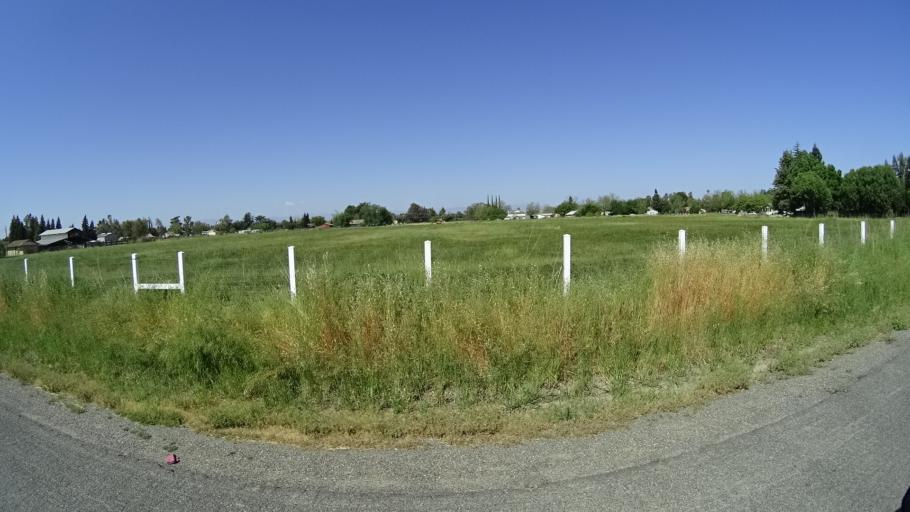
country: US
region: California
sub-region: Glenn County
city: Orland
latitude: 39.7353
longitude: -122.1827
